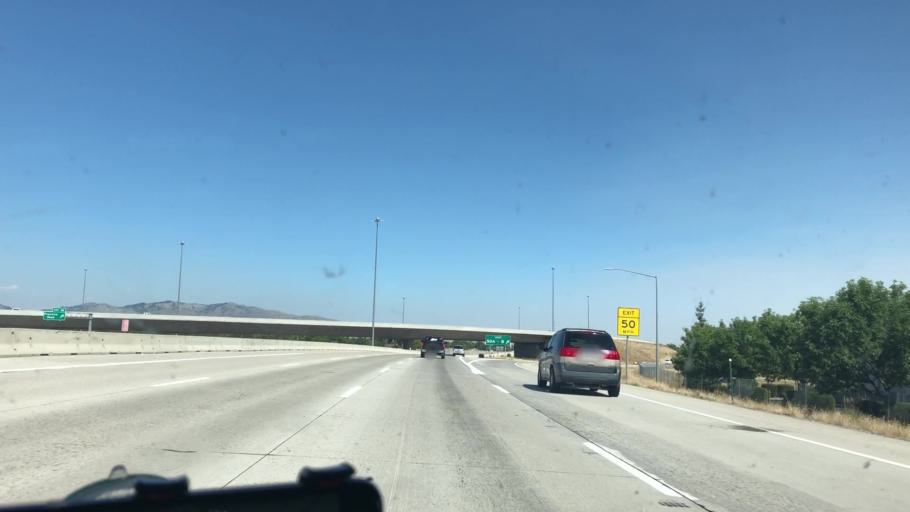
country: US
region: Idaho
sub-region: Ada County
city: Garden City
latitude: 43.5968
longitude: -116.2925
